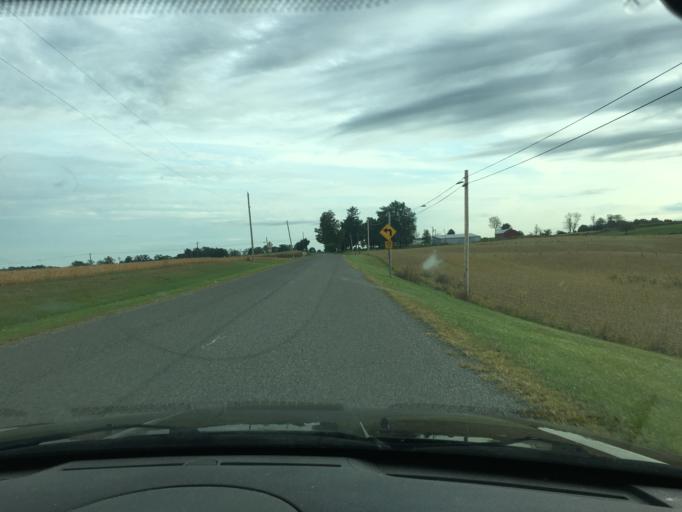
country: US
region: Ohio
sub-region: Logan County
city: West Liberty
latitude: 40.2984
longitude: -83.6848
